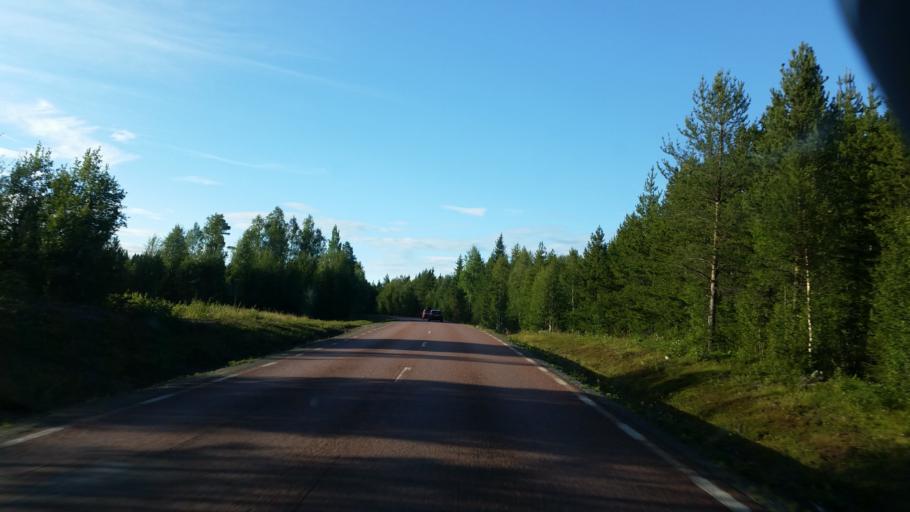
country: SE
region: Vaesterbotten
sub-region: Dorotea Kommun
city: Dorotea
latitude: 64.0791
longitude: 16.0875
